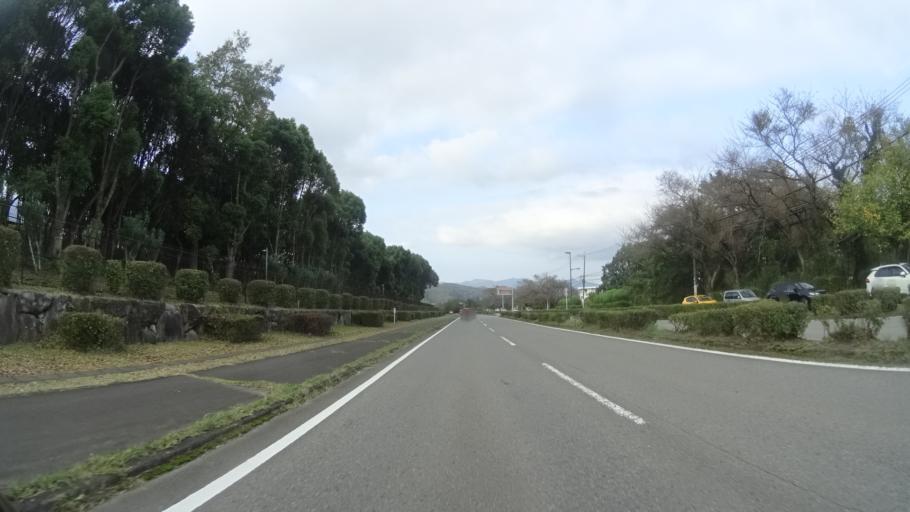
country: JP
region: Oita
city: Beppu
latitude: 33.2968
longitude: 131.4610
